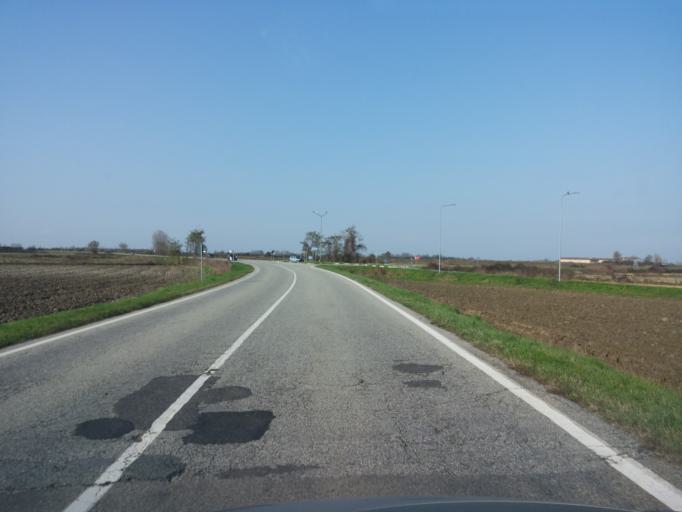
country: IT
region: Piedmont
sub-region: Provincia di Vercelli
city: Caresana
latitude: 45.2233
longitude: 8.4965
